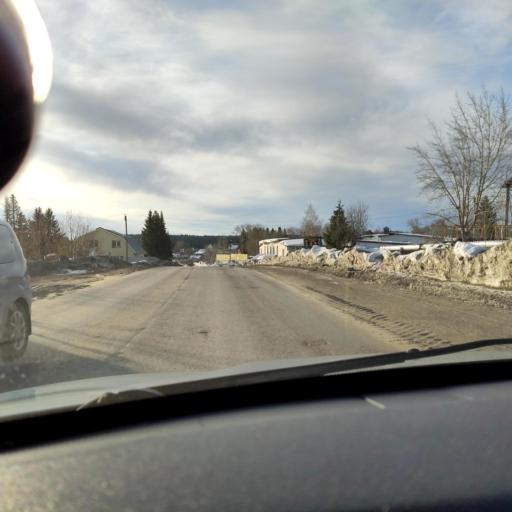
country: RU
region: Perm
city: Polazna
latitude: 58.2885
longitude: 56.4071
